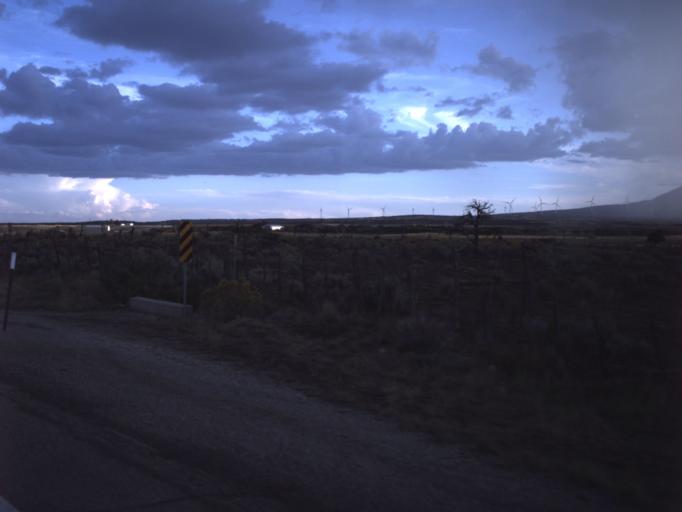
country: US
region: Utah
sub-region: San Juan County
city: Monticello
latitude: 37.9538
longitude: -109.3487
